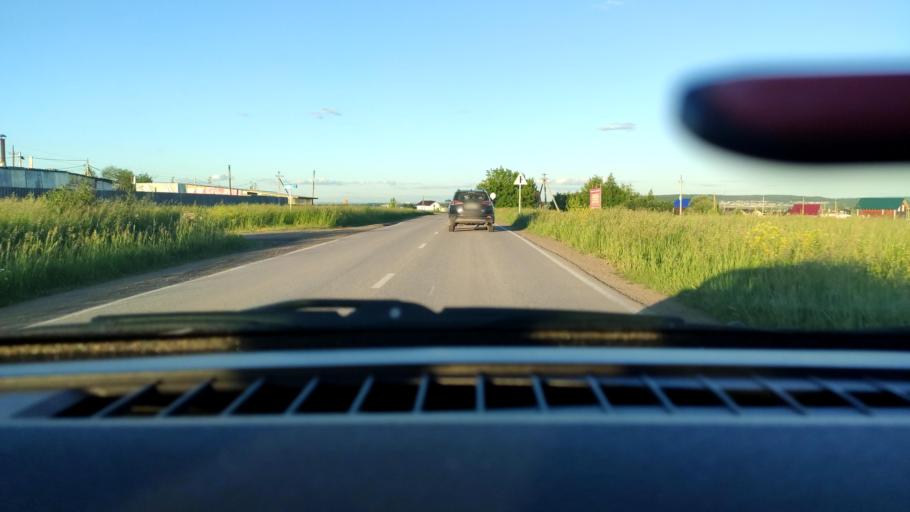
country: RU
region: Perm
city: Kultayevo
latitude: 57.9199
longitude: 55.9417
